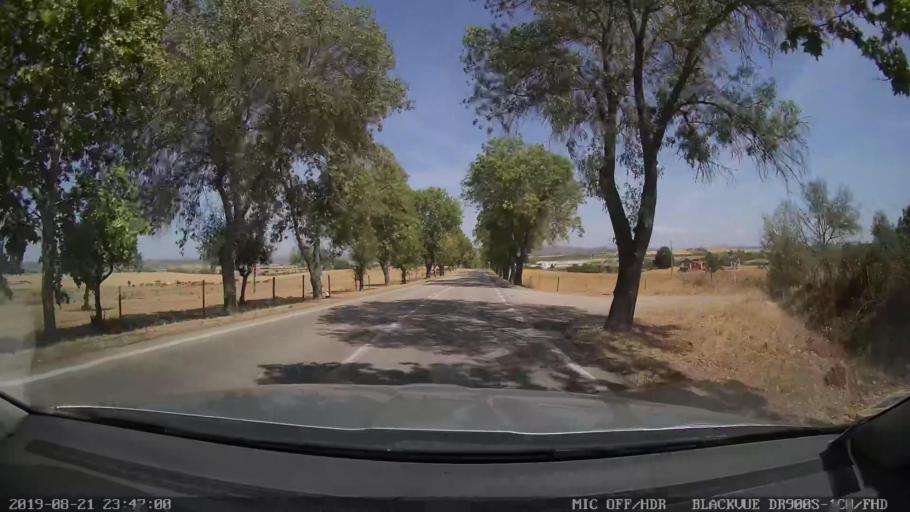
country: PT
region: Castelo Branco
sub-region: Idanha-A-Nova
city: Idanha-a-Nova
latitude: 39.8461
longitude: -7.2569
